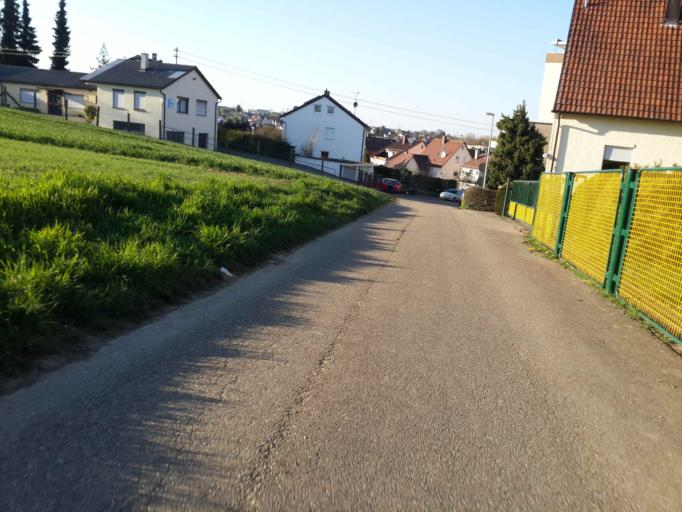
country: DE
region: Baden-Wuerttemberg
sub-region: Regierungsbezirk Stuttgart
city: Heilbronn
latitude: 49.1547
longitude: 9.1754
